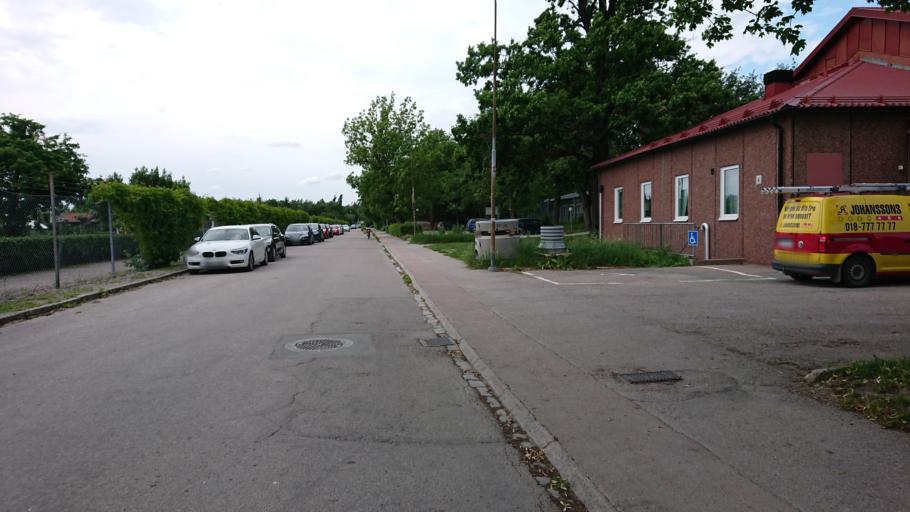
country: SE
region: Uppsala
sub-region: Uppsala Kommun
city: Uppsala
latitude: 59.8755
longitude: 17.6145
